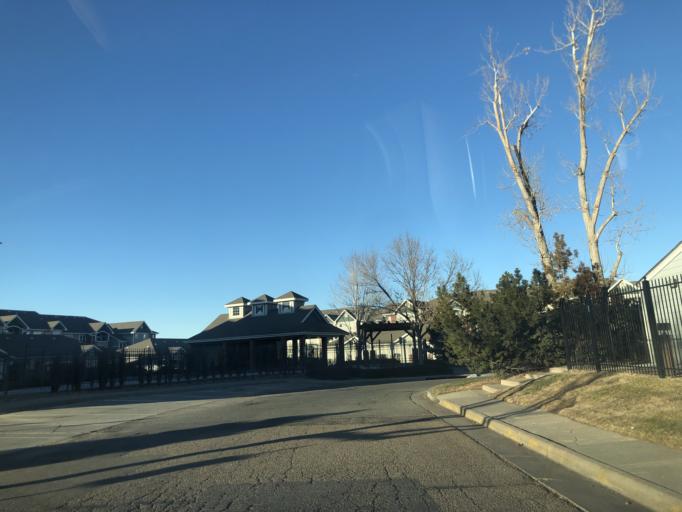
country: US
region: Colorado
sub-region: Adams County
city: Aurora
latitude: 39.7181
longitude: -104.8223
